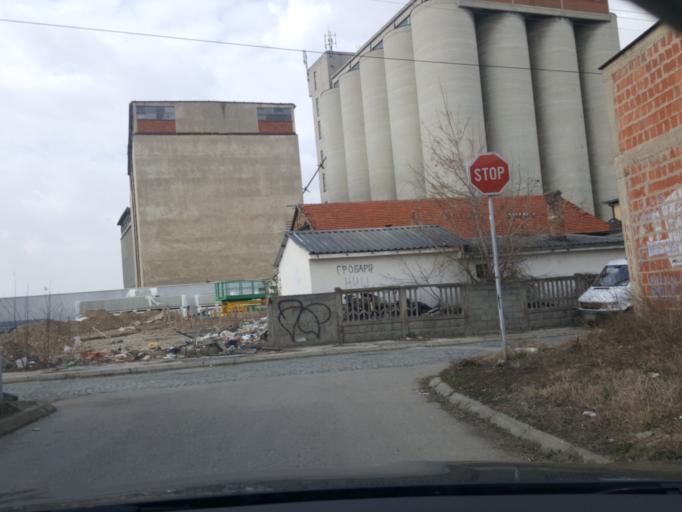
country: RS
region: Central Serbia
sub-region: Nisavski Okrug
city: Nis
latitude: 43.3146
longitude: 21.8745
